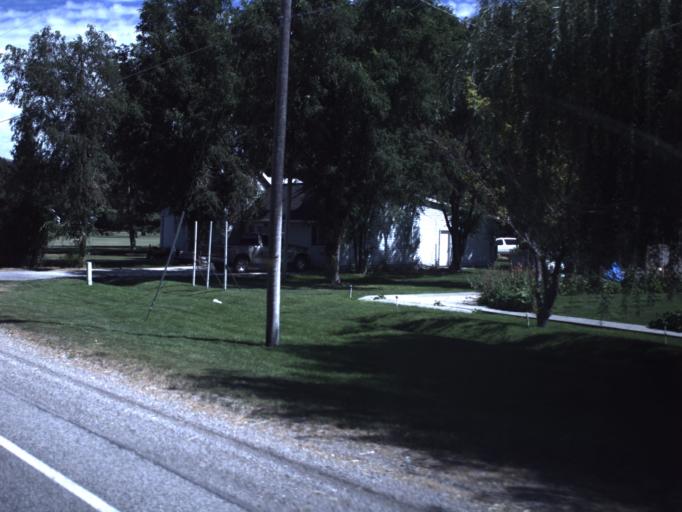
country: US
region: Utah
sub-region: Box Elder County
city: Garland
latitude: 41.7876
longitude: -112.1494
